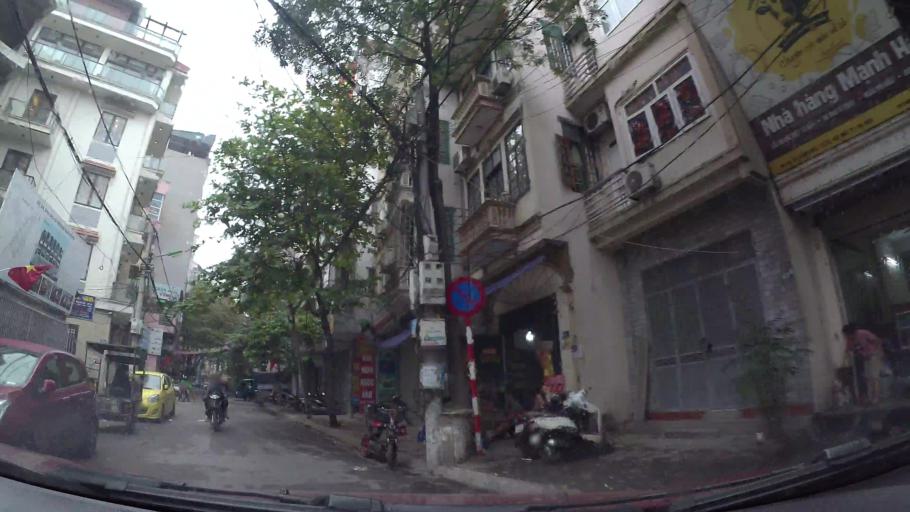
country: VN
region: Ha Noi
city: Dong Da
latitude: 21.0142
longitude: 105.8304
